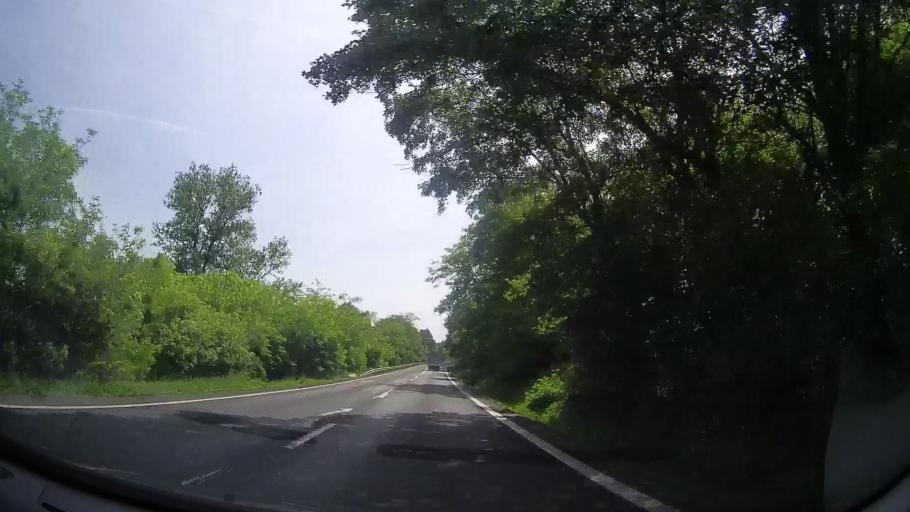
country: RO
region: Hunedoara
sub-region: Comuna Branisca
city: Branisca
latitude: 45.9198
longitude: 22.7174
